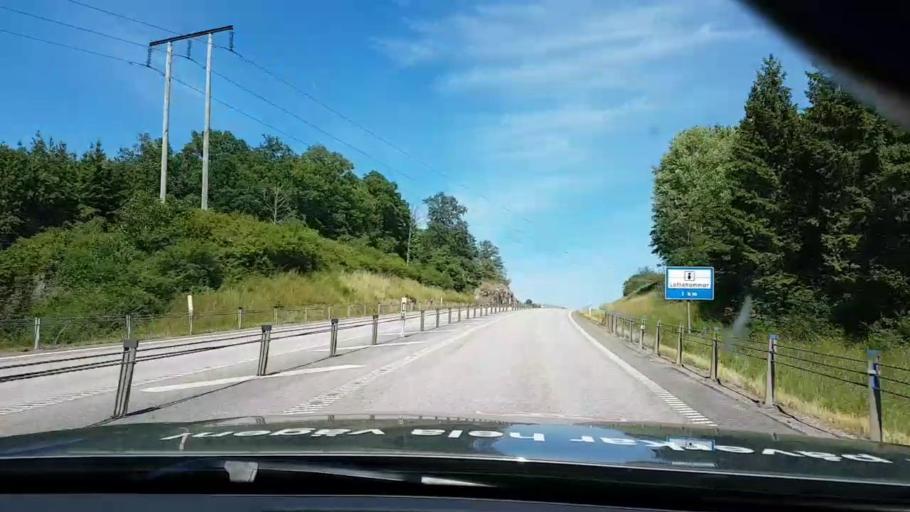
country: SE
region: Kalmar
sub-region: Vasterviks Kommun
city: Gamleby
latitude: 57.9348
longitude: 16.4126
